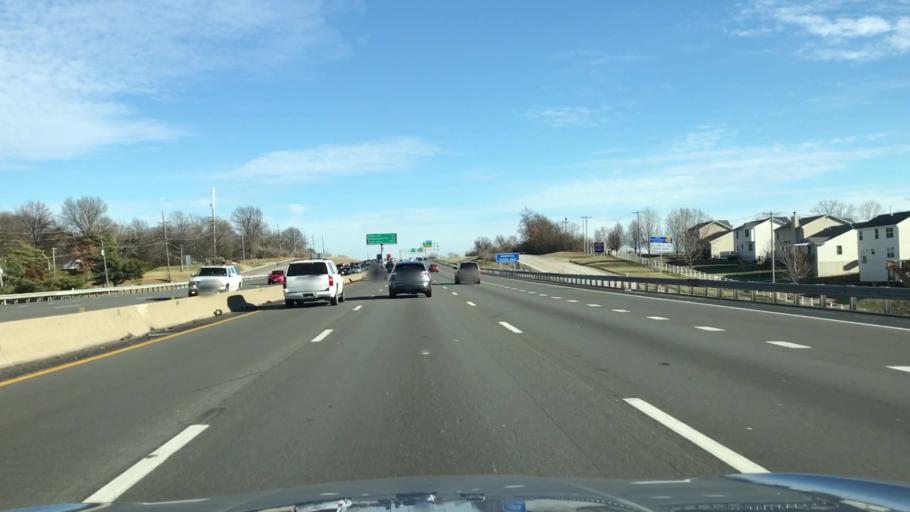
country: US
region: Missouri
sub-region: Saint Louis County
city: Castle Point
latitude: 38.7708
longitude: -90.2506
